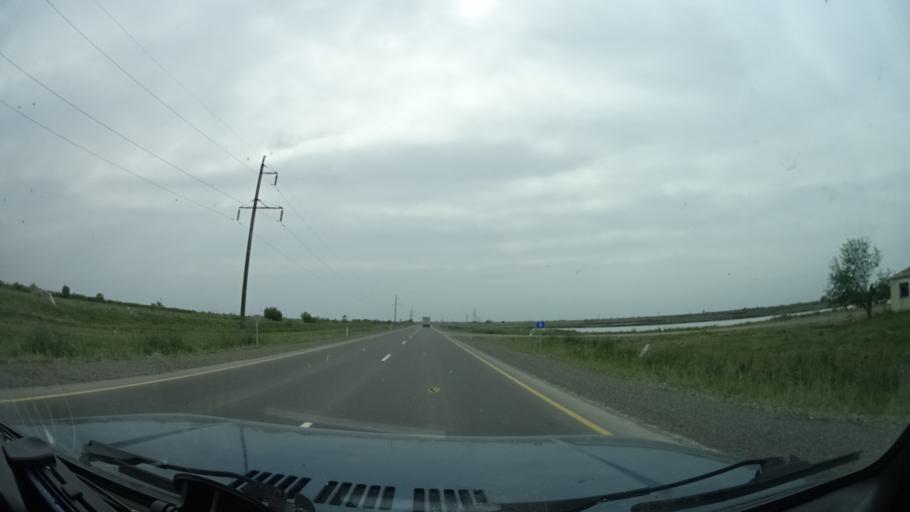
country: AZ
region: Beylaqan
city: Dunyamalilar
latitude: 39.7805
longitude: 47.8155
